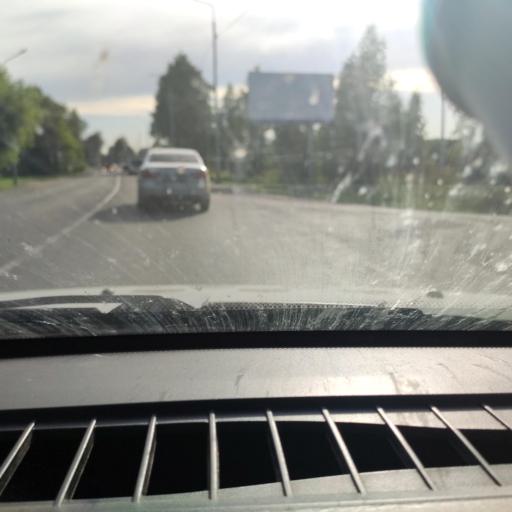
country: RU
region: Kirov
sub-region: Kirovo-Chepetskiy Rayon
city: Kirov
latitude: 58.6160
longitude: 49.7598
